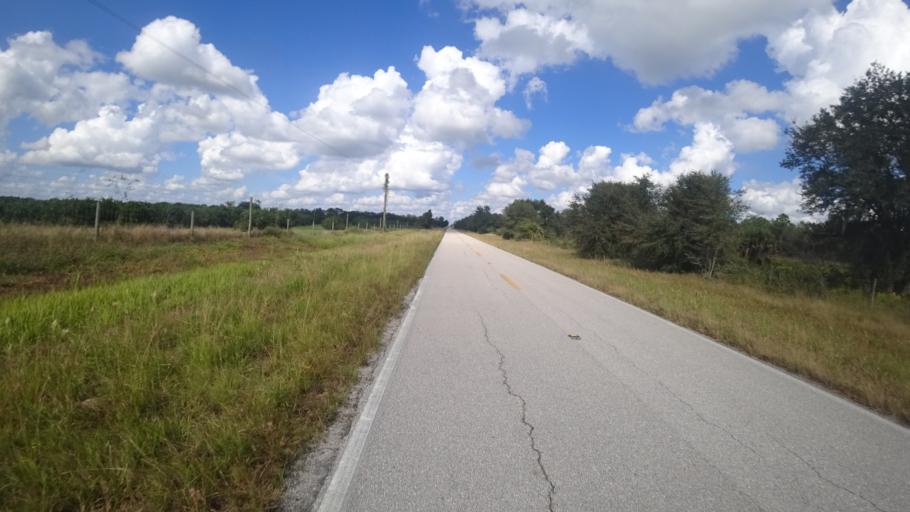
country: US
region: Florida
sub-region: Sarasota County
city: North Port
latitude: 27.2311
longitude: -82.1220
